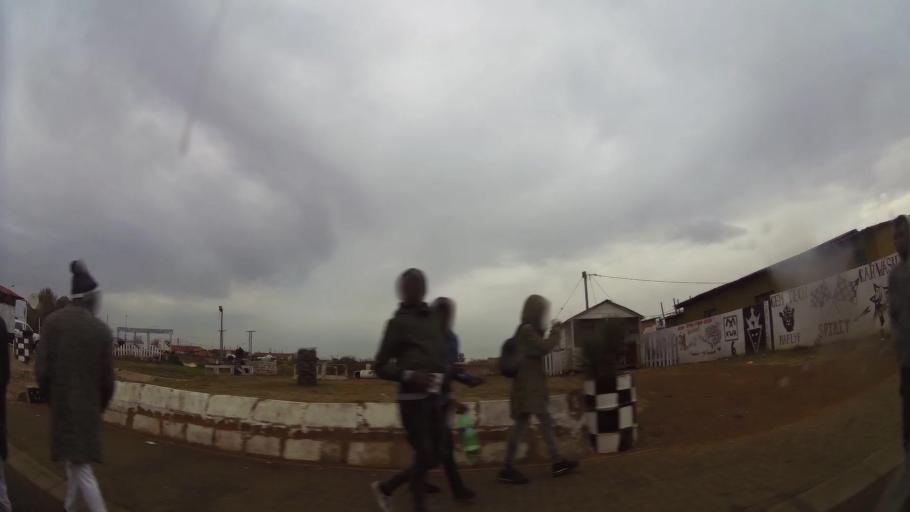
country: ZA
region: Gauteng
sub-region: Ekurhuleni Metropolitan Municipality
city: Germiston
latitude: -26.3795
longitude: 28.1786
